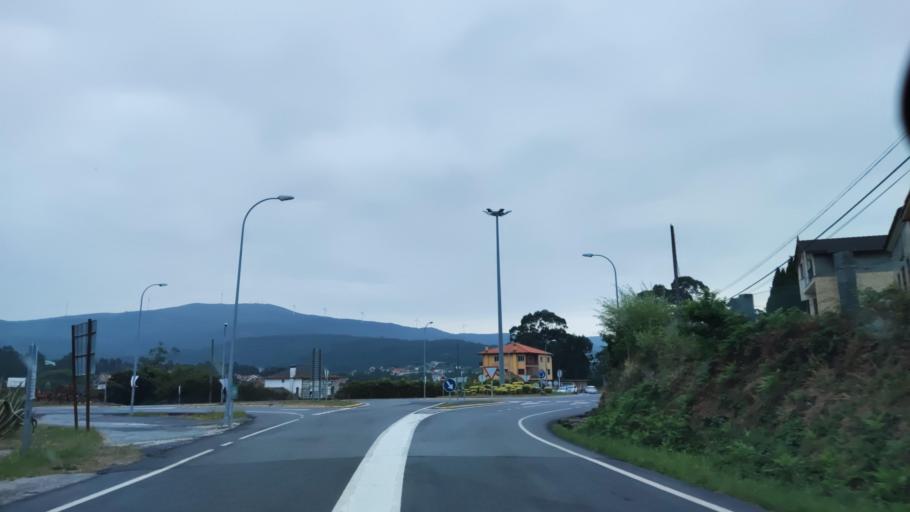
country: ES
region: Galicia
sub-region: Provincia de Pontevedra
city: Catoira
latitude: 42.6777
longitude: -8.7295
